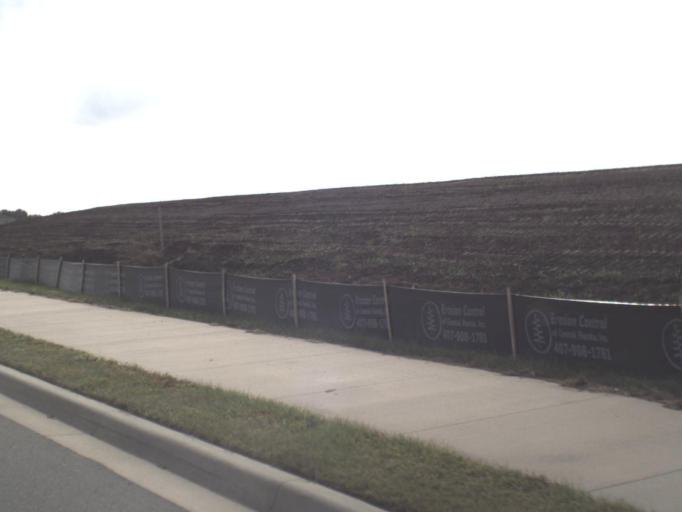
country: US
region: Florida
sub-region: Osceola County
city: Saint Cloud
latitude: 28.2570
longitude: -81.2418
